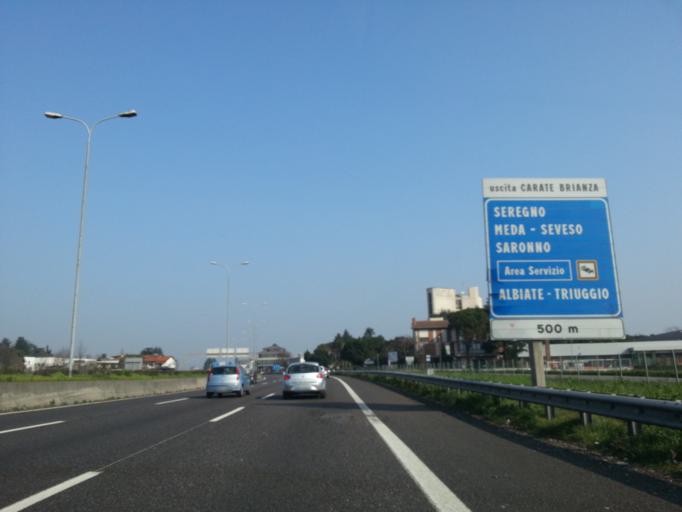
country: IT
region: Lombardy
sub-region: Provincia di Monza e Brianza
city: Carate Brianza
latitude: 45.6546
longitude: 9.2261
